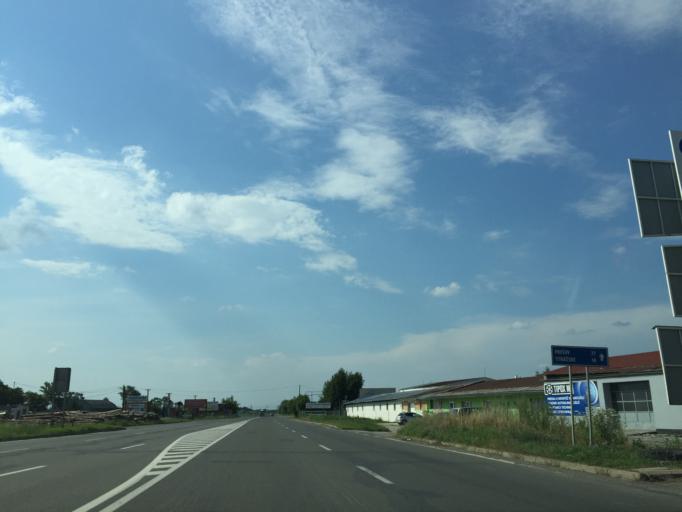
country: SK
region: Kosicky
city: Michalovce
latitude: 48.7557
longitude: 21.8963
